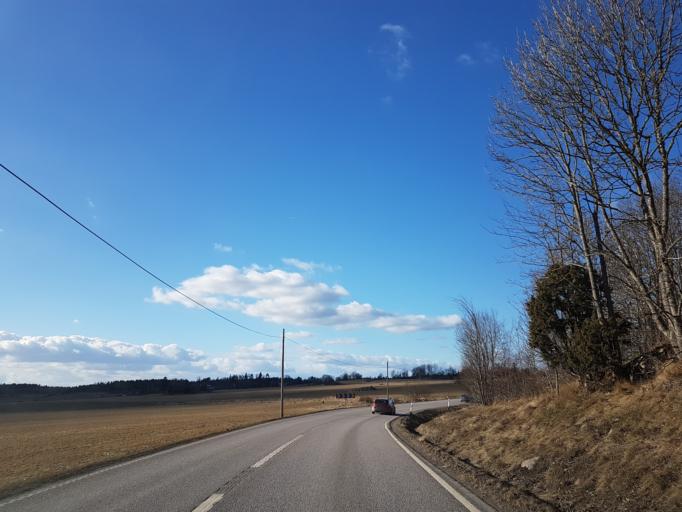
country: SE
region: Stockholm
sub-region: Norrtalje Kommun
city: Rimbo
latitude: 59.7378
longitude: 18.5281
